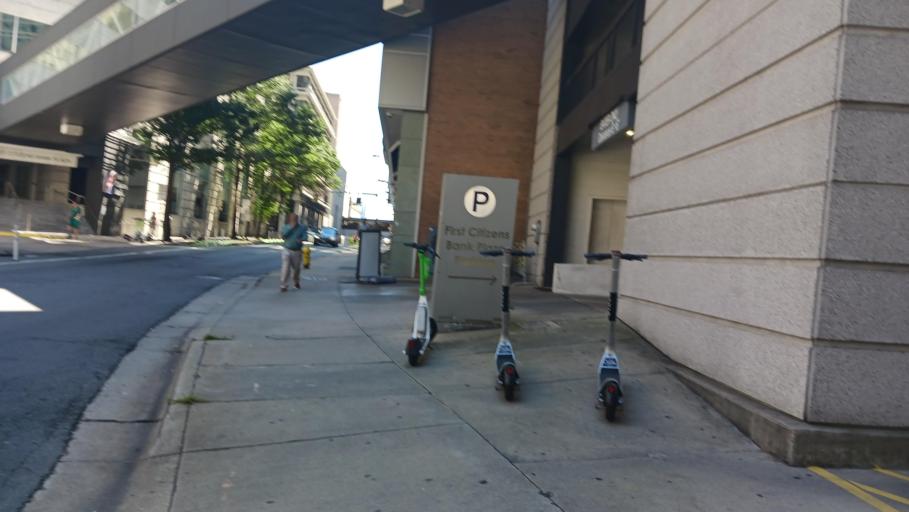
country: US
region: North Carolina
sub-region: Mecklenburg County
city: Charlotte
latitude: 35.2272
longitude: -80.8453
